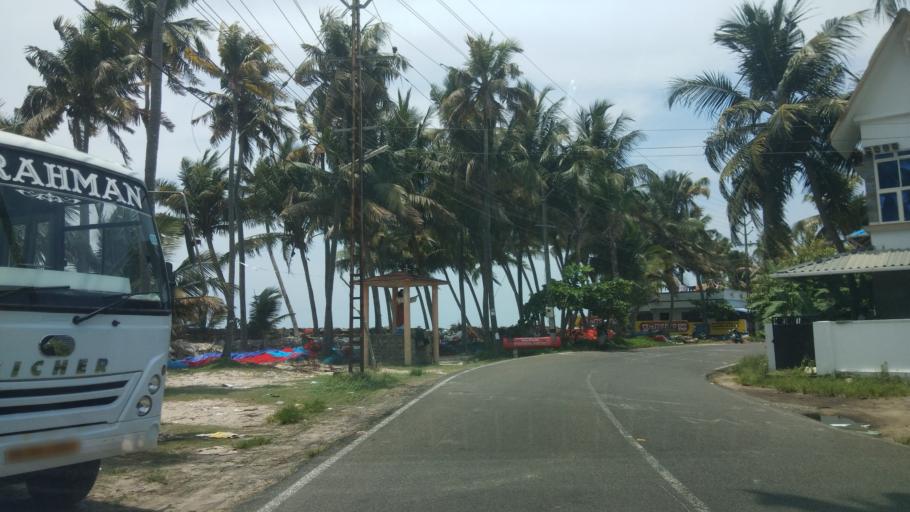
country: IN
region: Kerala
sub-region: Alappuzha
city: Arukutti
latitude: 9.8540
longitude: 76.2656
